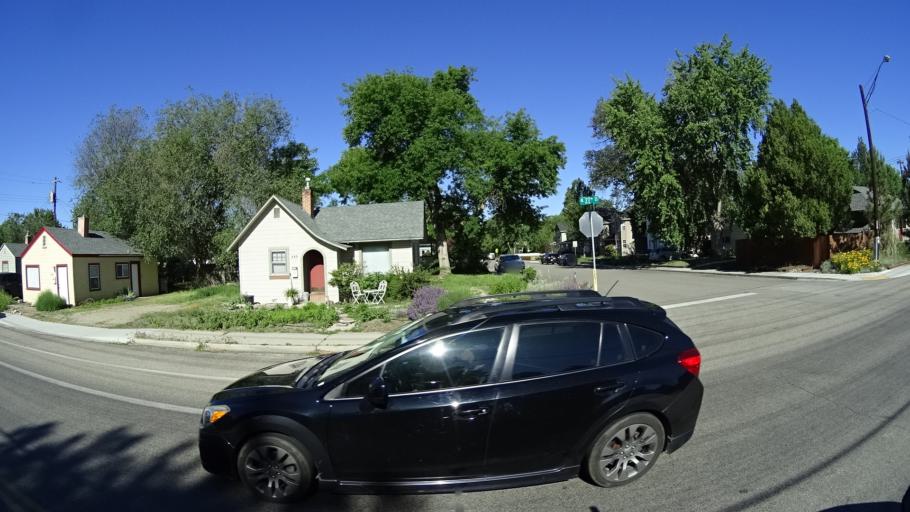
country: US
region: Idaho
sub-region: Ada County
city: Garden City
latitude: 43.6252
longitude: -116.2239
